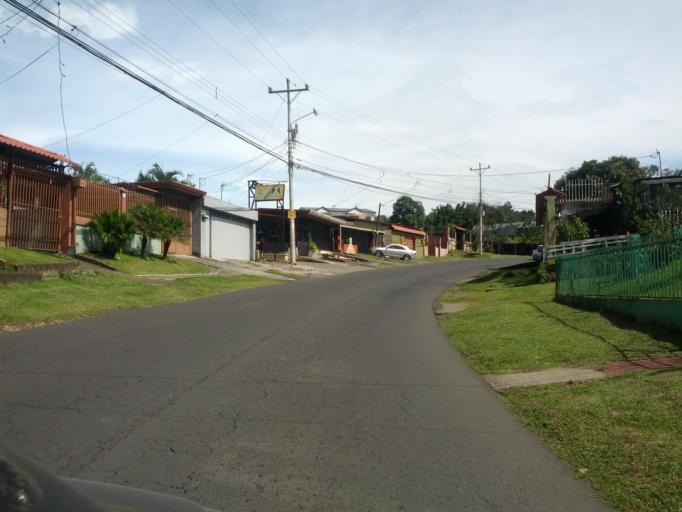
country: CR
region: Alajuela
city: Alajuela
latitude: 10.0274
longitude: -84.1825
